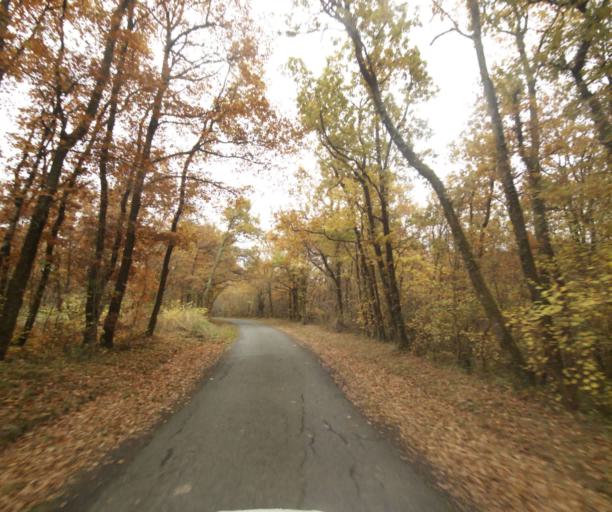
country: FR
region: Poitou-Charentes
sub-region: Departement de la Charente-Maritime
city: Chermignac
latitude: 45.7092
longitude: -0.6710
